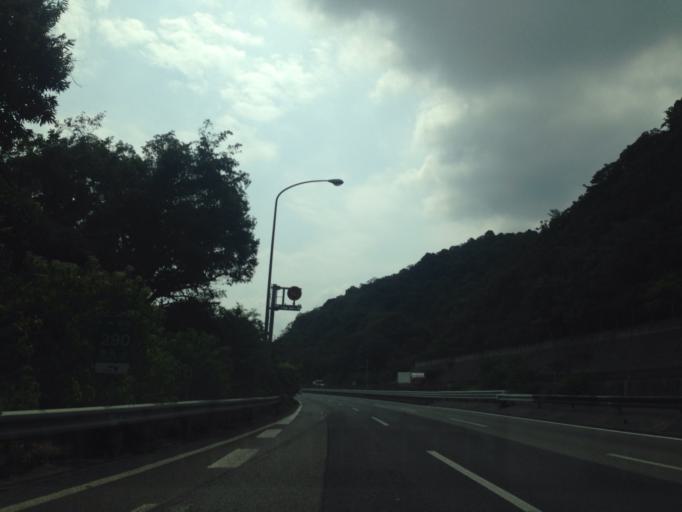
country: JP
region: Aichi
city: Okazaki
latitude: 34.9249
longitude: 137.2258
